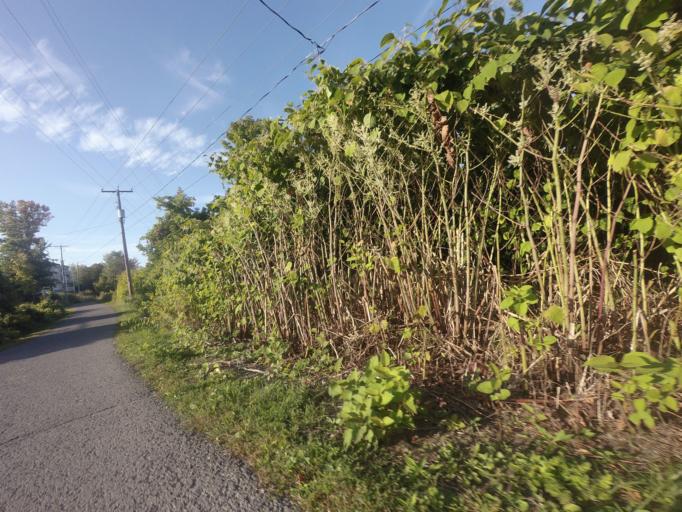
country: CA
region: Quebec
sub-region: Laurentides
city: Saint-Jerome
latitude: 45.7706
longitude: -73.9976
